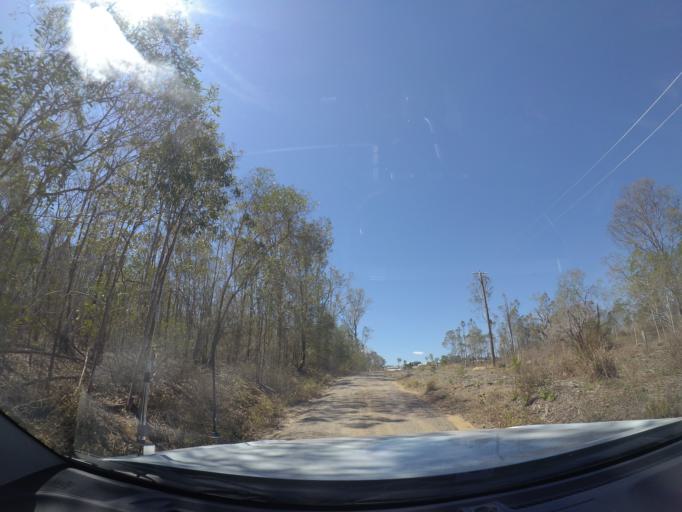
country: AU
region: Queensland
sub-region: Logan
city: North Maclean
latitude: -27.7609
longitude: 152.9416
